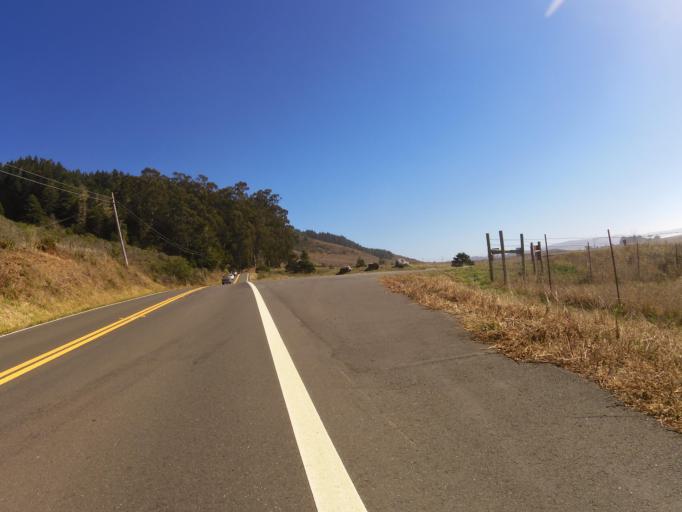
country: US
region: California
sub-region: Mendocino County
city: Fort Bragg
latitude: 39.5877
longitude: -123.7752
